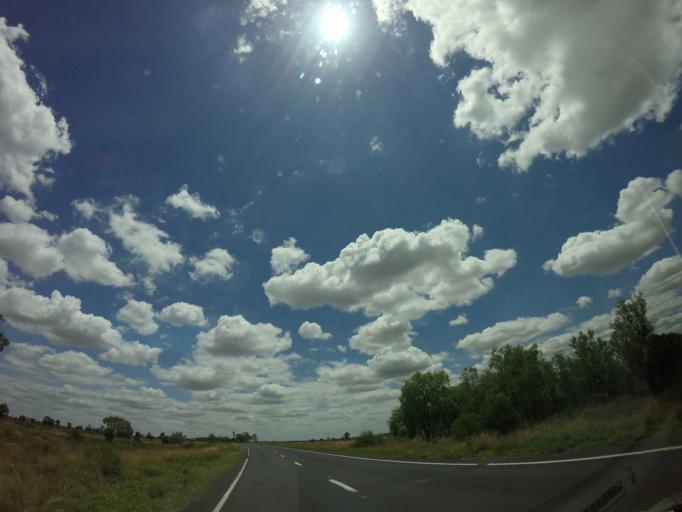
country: AU
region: New South Wales
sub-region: Moree Plains
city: Boggabilla
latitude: -28.7267
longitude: 150.2759
